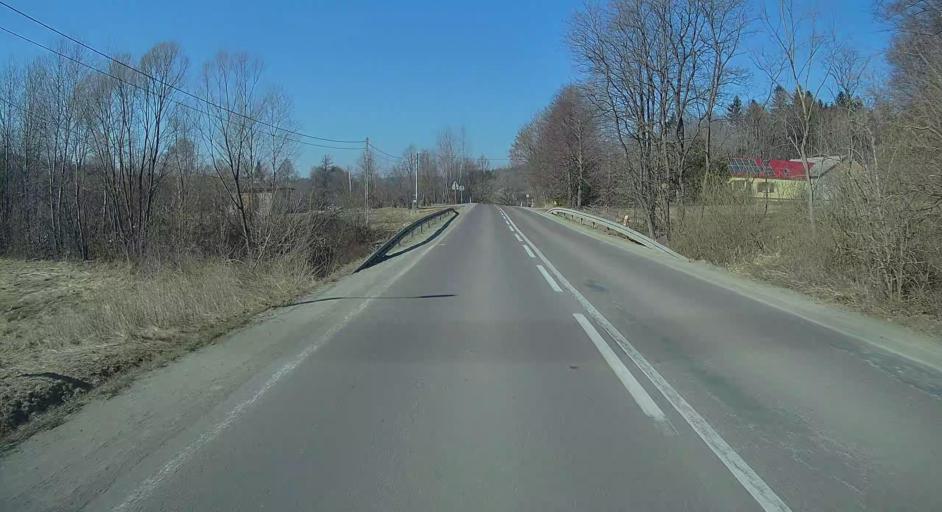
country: PL
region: Subcarpathian Voivodeship
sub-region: Powiat bieszczadzki
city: Ustrzyki Dolne
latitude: 49.5348
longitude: 22.5975
